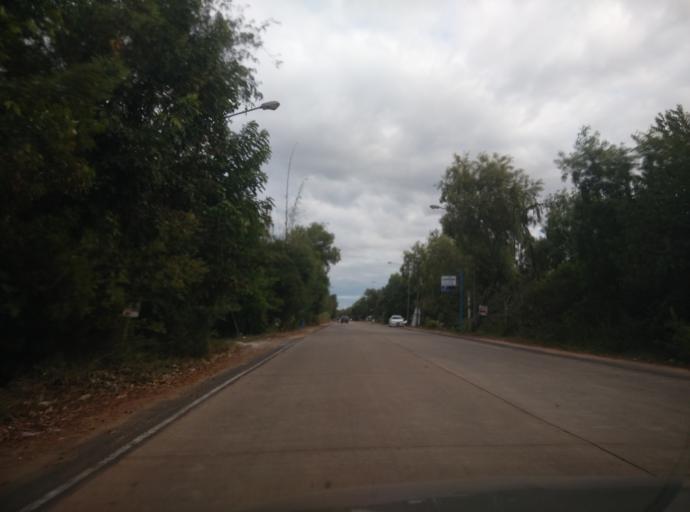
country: TH
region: Sisaket
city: Si Sa Ket
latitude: 15.1226
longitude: 104.3469
